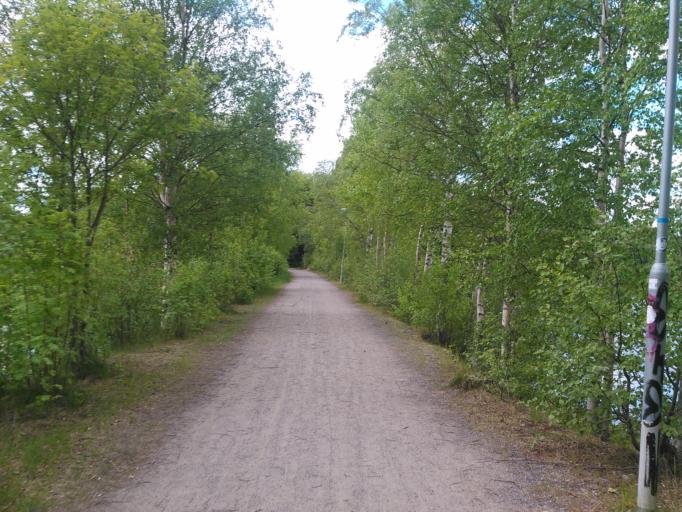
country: SE
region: Vaesterbotten
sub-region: Umea Kommun
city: Umea
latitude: 63.8256
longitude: 20.2325
